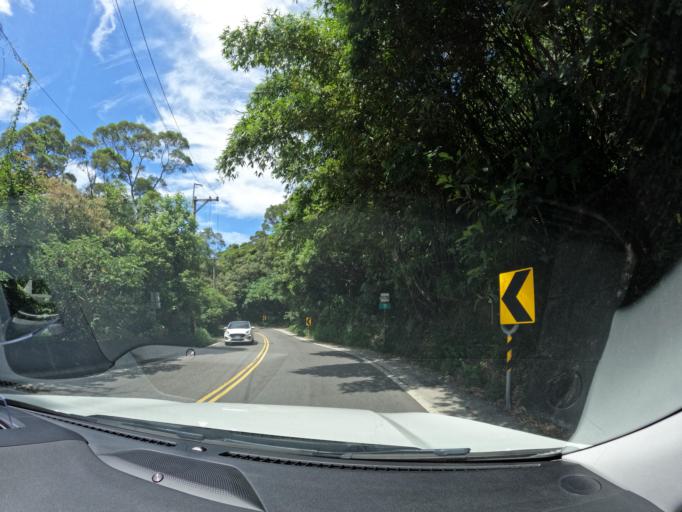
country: TW
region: Taipei
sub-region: Taipei
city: Banqiao
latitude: 25.1195
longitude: 121.3886
